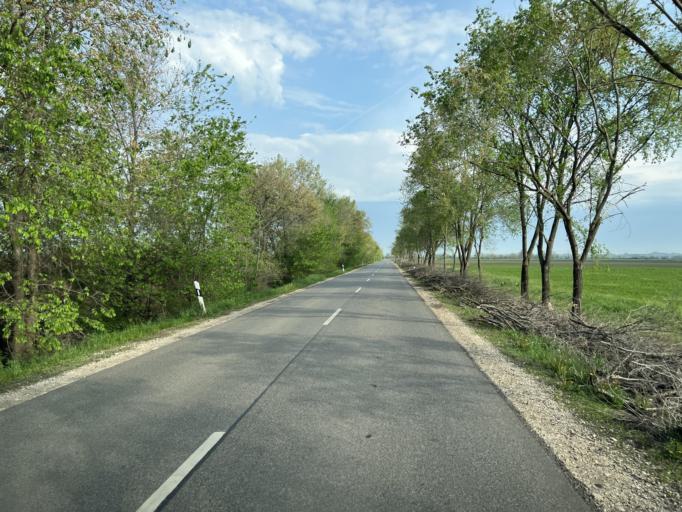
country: HU
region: Pest
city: Cegled
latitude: 47.2218
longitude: 19.7728
